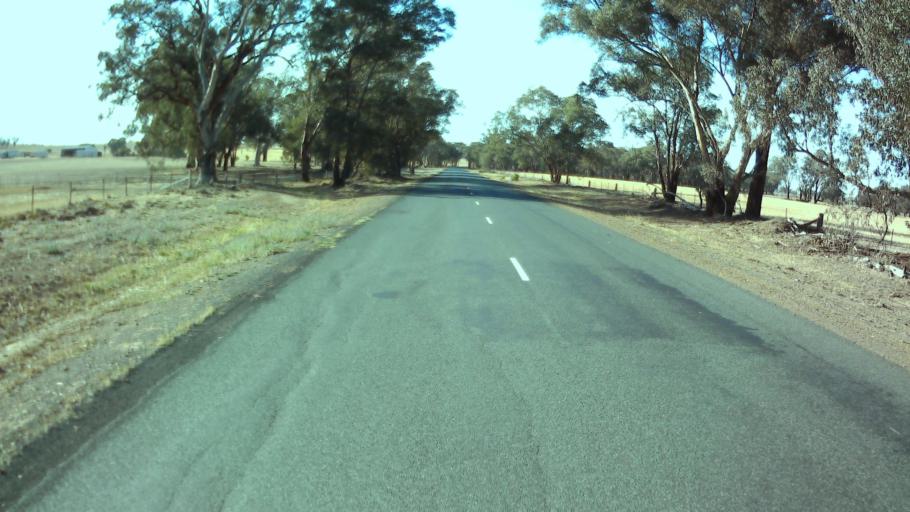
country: AU
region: New South Wales
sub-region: Weddin
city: Grenfell
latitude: -33.9463
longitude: 148.1362
